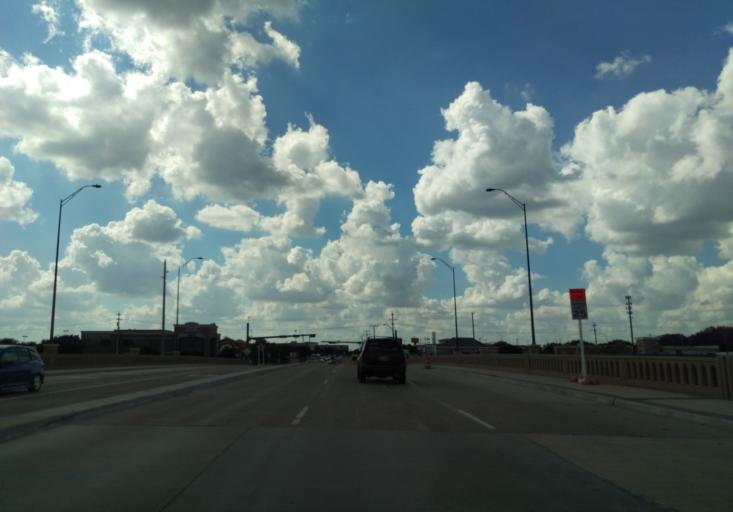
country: US
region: Texas
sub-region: Brazos County
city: College Station
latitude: 30.5852
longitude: -96.2846
